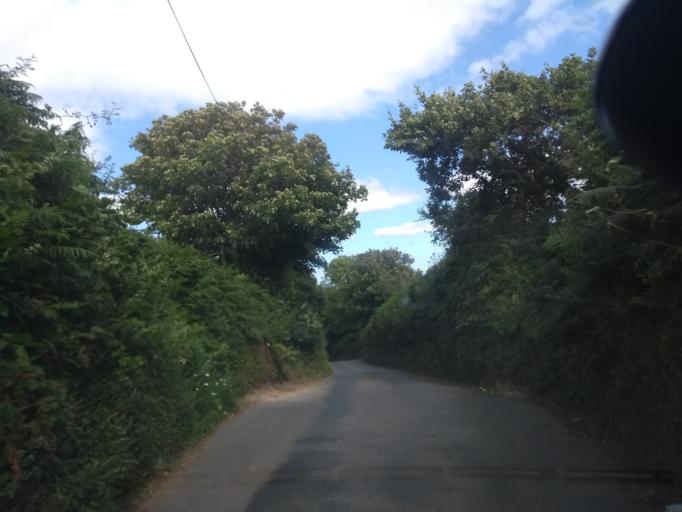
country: GB
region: England
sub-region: Devon
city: Modbury
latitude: 50.3063
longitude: -3.8628
